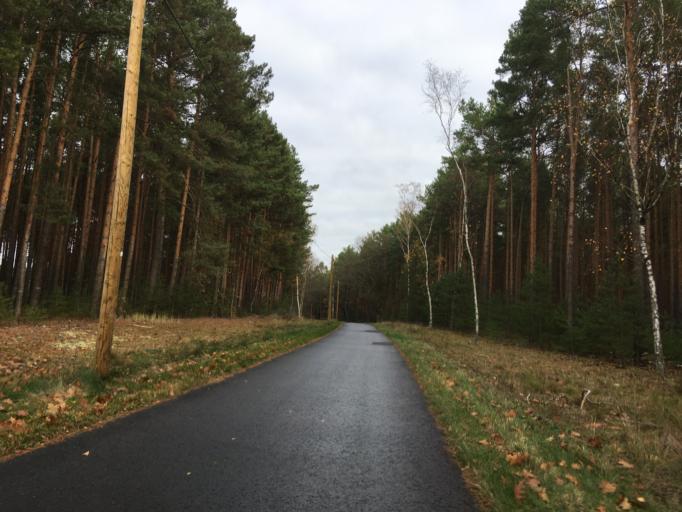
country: DE
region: Brandenburg
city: Tauer
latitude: 51.9114
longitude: 14.4643
